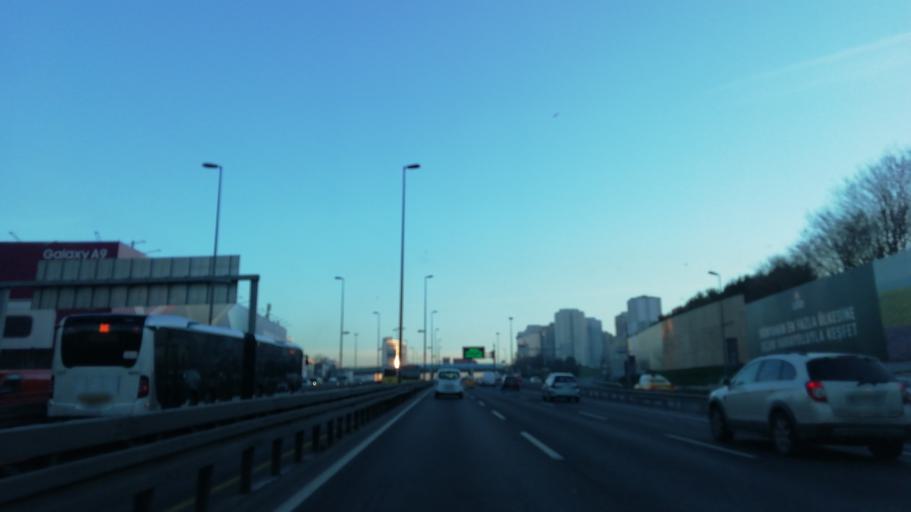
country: TR
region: Istanbul
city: guengoeren merter
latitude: 41.0103
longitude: 28.9012
